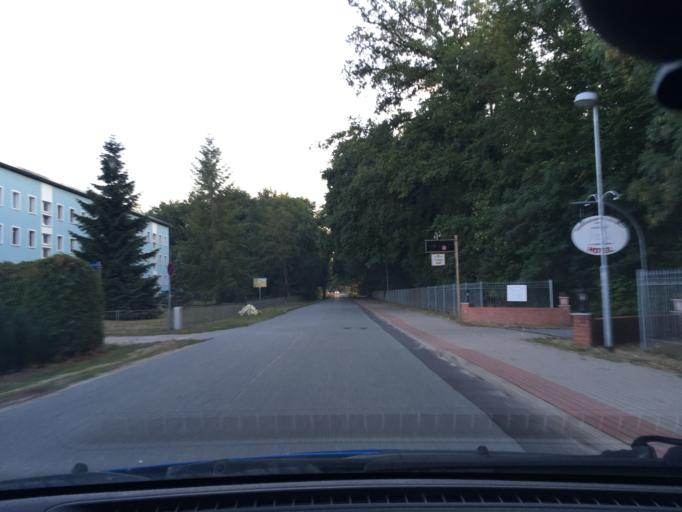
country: DE
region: Mecklenburg-Vorpommern
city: Boizenburg
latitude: 53.3968
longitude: 10.7455
